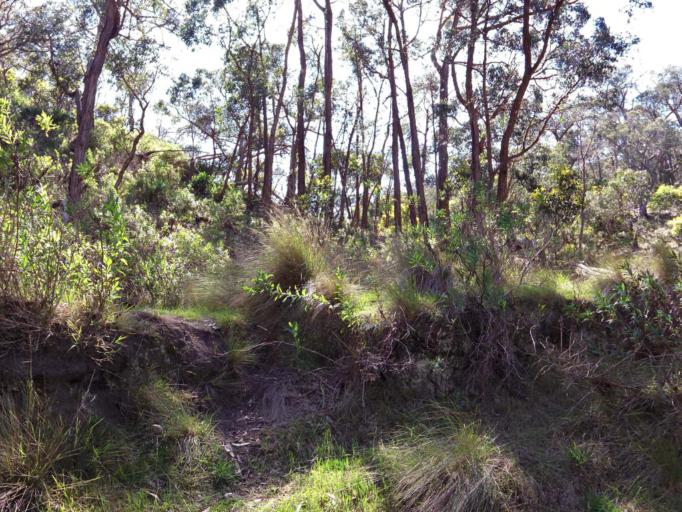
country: AU
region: Victoria
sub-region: Moorabool
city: Bacchus Marsh
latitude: -37.6638
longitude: 144.3146
